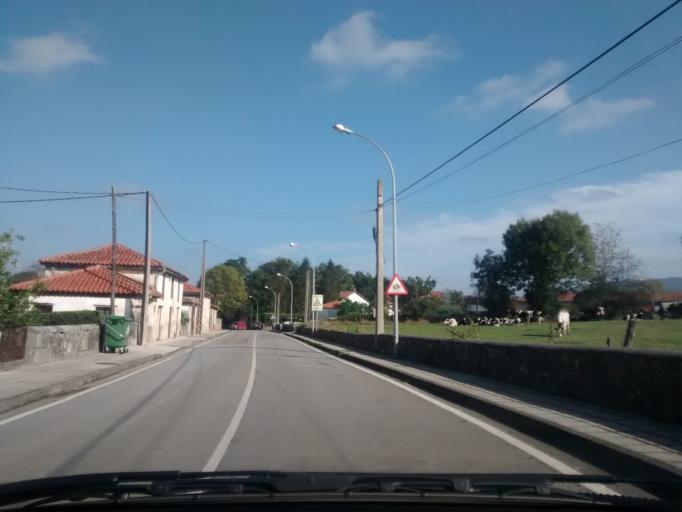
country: ES
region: Cantabria
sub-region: Provincia de Cantabria
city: Entrambasaguas
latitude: 43.3752
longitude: -3.6834
